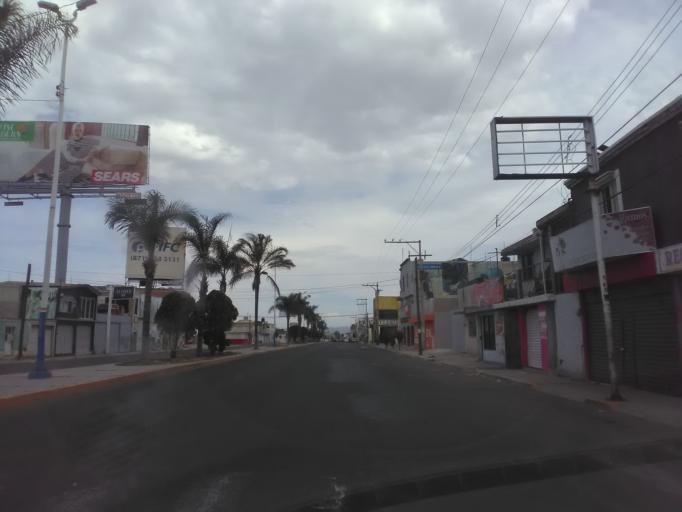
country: MX
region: Durango
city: Victoria de Durango
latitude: 24.0194
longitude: -104.6601
